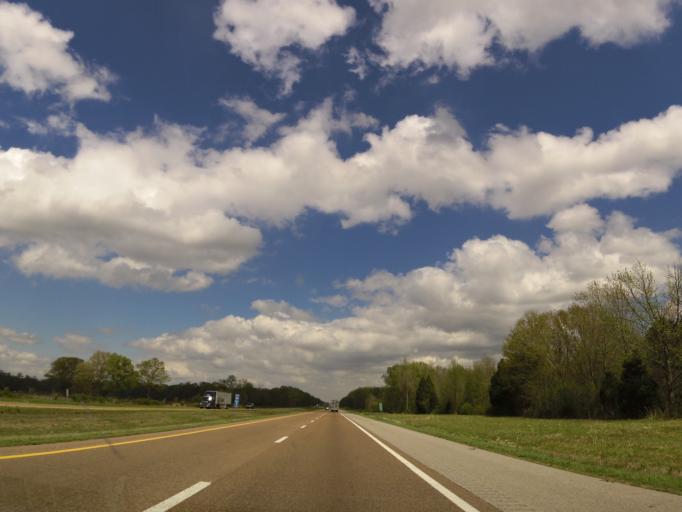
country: US
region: Tennessee
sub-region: Shelby County
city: Arlington
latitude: 35.2922
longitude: -89.6096
